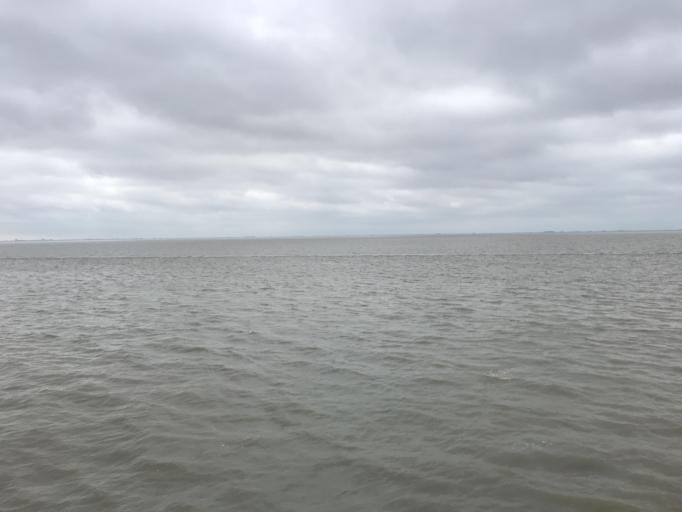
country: DE
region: Lower Saxony
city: Emden
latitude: 53.3311
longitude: 7.1410
